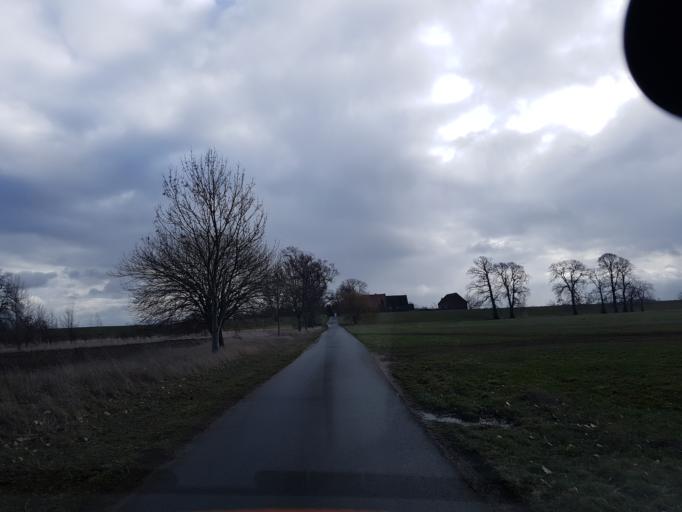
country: DE
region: Brandenburg
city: Muhlberg
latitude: 51.4842
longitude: 13.1895
